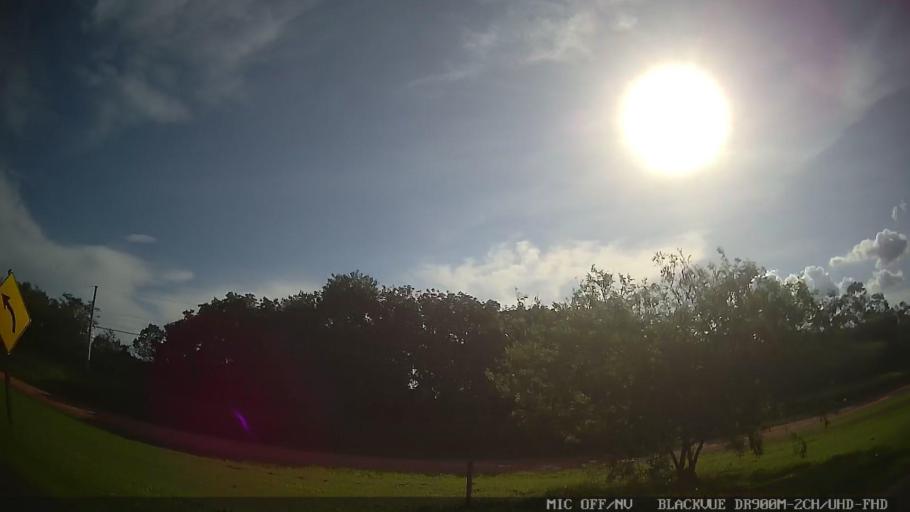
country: BR
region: Sao Paulo
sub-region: Tiete
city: Tiete
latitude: -23.0992
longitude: -47.7739
